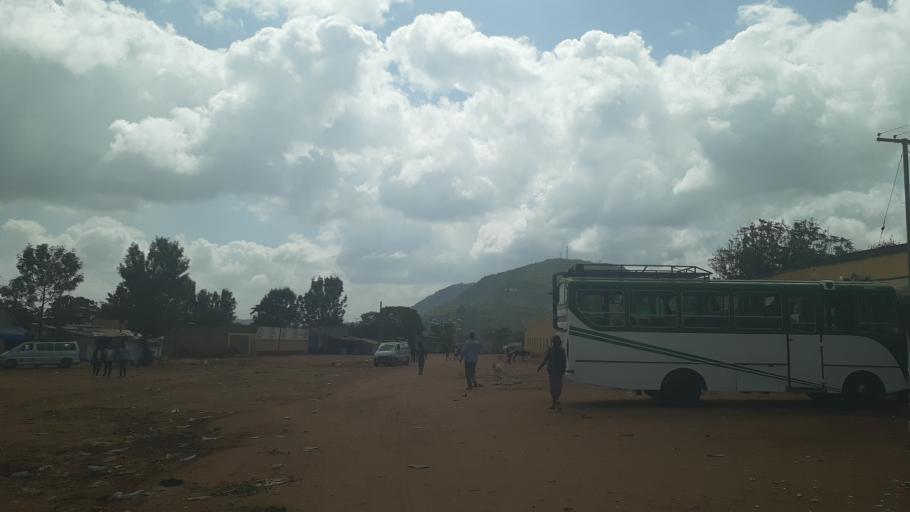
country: ET
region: Oromiya
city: Yabelo
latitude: 4.8988
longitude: 38.0892
